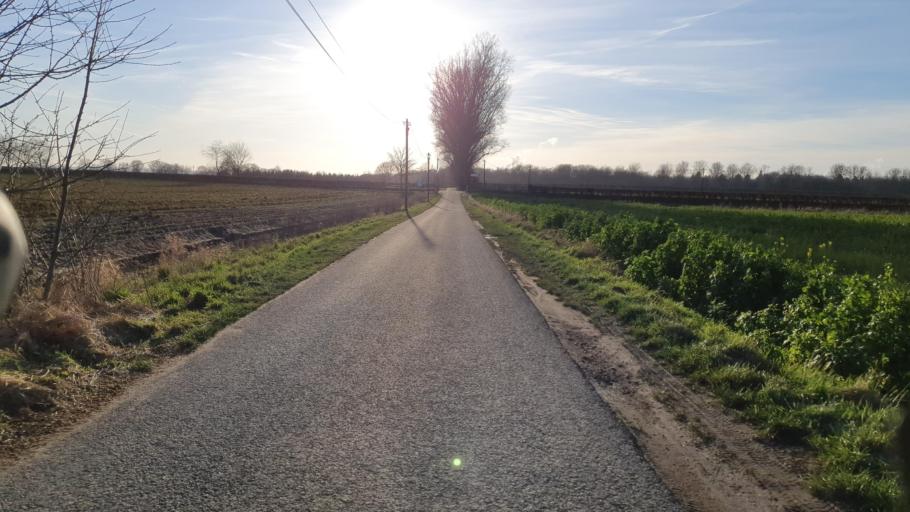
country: DE
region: North Rhine-Westphalia
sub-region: Regierungsbezirk Koln
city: Sinnersdorf
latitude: 51.0485
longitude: 6.8230
